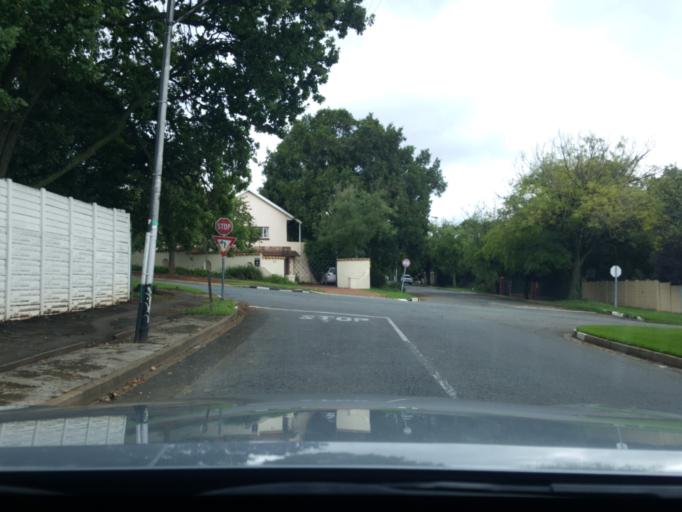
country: ZA
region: Gauteng
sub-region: City of Johannesburg Metropolitan Municipality
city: Johannesburg
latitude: -26.1286
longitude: 28.0023
